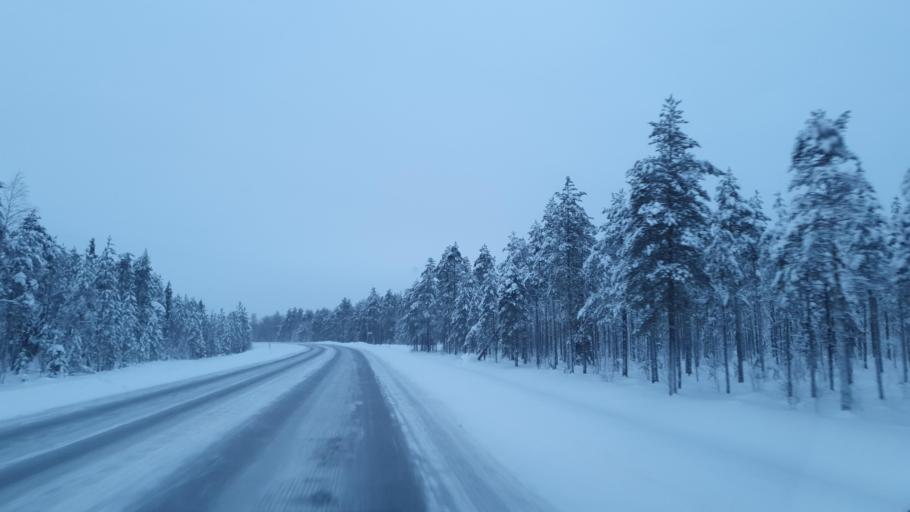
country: FI
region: Kainuu
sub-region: Kajaani
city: Vaala
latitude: 64.5915
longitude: 26.8050
